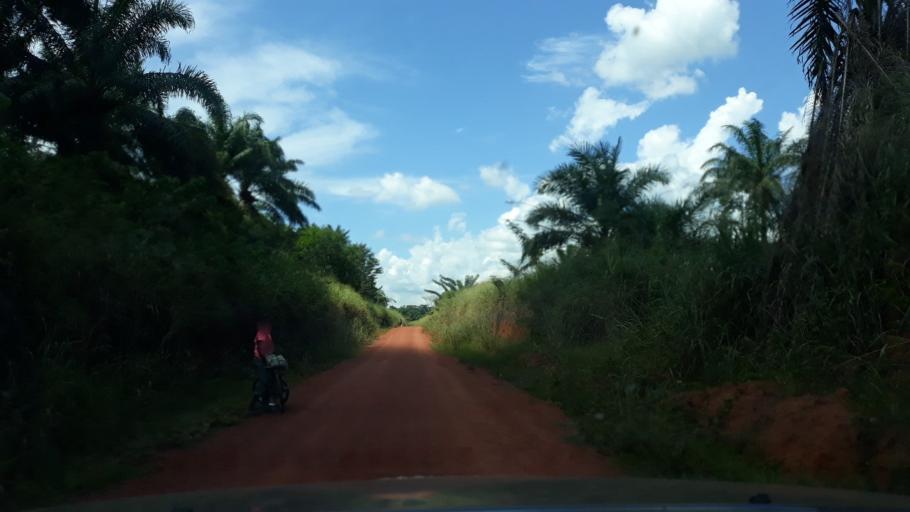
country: CD
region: Equateur
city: Businga
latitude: 3.4047
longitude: 20.3881
